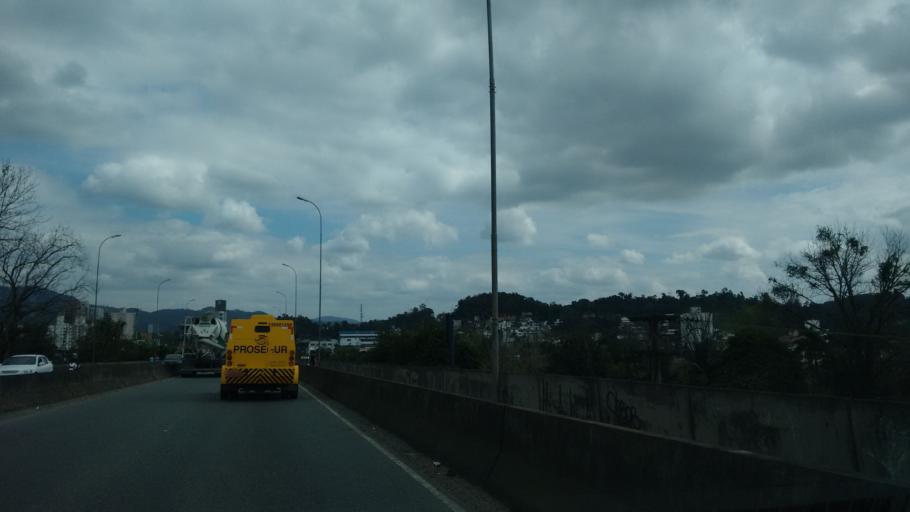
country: BR
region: Santa Catarina
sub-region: Blumenau
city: Blumenau
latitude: -26.8964
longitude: -49.0748
